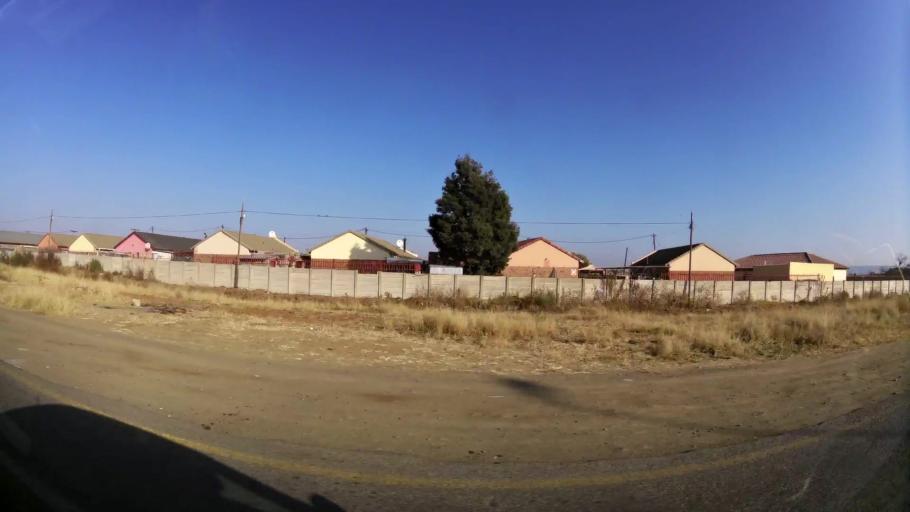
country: ZA
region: Orange Free State
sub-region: Mangaung Metropolitan Municipality
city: Bloemfontein
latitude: -29.1484
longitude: 26.2655
